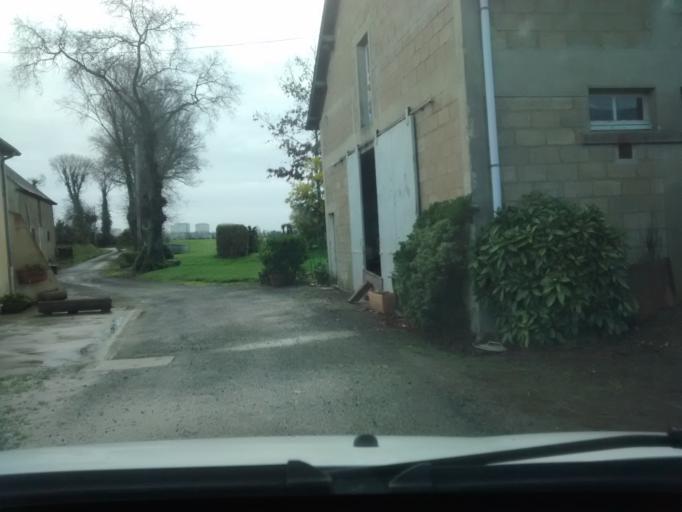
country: FR
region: Brittany
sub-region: Departement d'Ille-et-Vilaine
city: Montgermont
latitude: 48.1328
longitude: -1.7216
